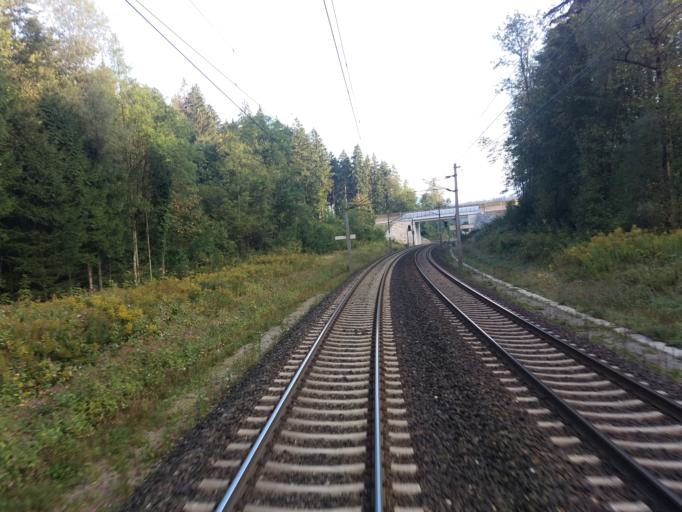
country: AT
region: Salzburg
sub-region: Politischer Bezirk Hallein
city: Adnet
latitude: 47.6611
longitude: 13.1235
